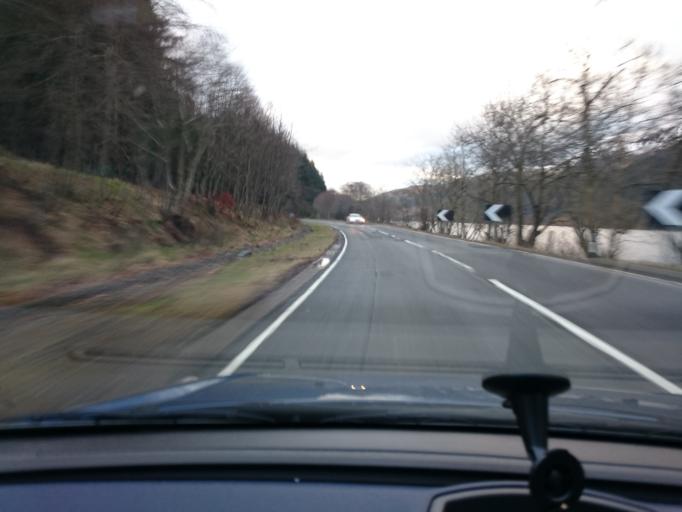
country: GB
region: Scotland
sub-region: Stirling
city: Callander
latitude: 56.2835
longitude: -4.2844
